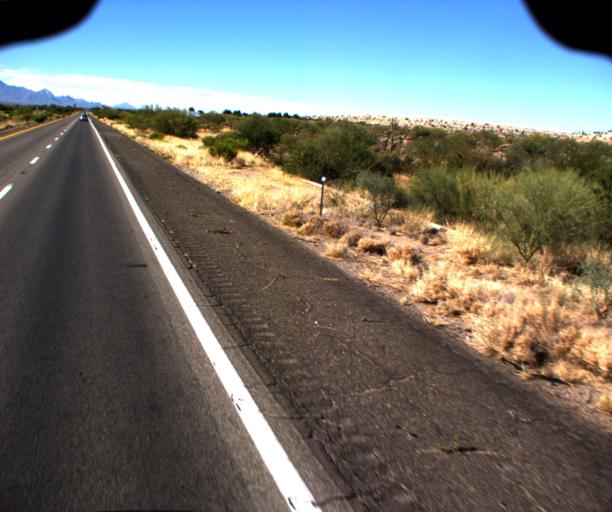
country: US
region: Arizona
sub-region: Pima County
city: Sahuarita
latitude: 31.9715
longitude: -110.9897
